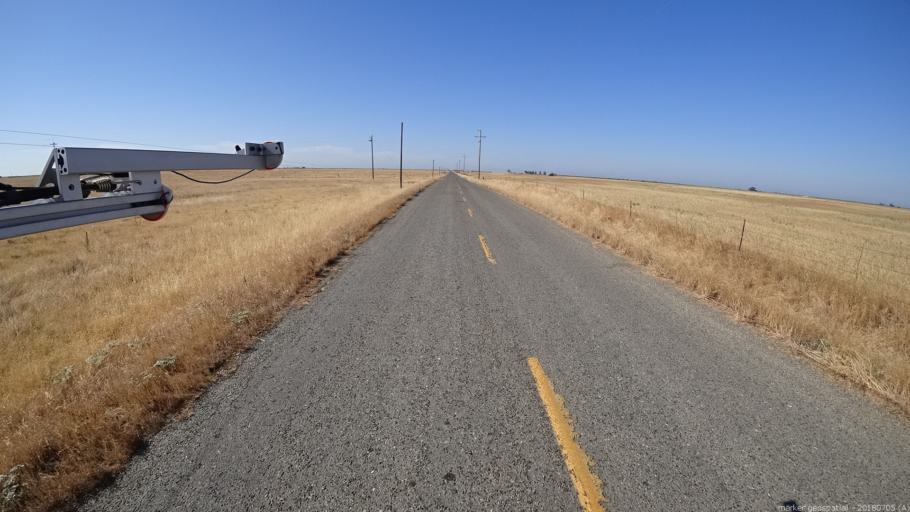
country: US
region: California
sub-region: Madera County
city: Madera Acres
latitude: 37.1421
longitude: -120.0747
